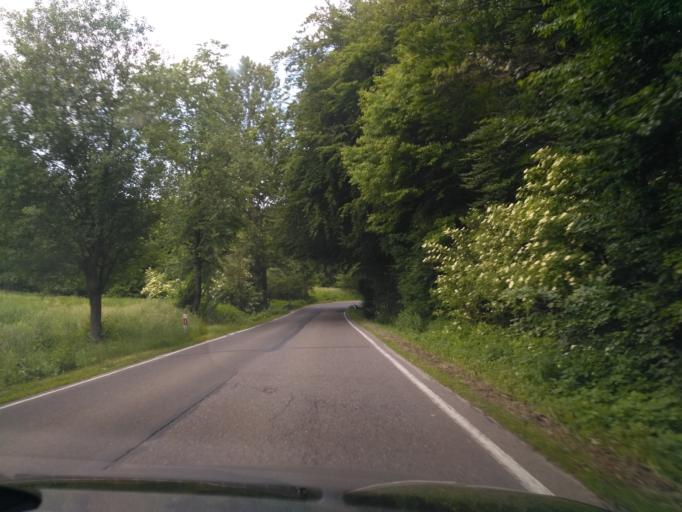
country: PL
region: Subcarpathian Voivodeship
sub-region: Powiat rzeszowski
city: Hyzne
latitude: 49.9423
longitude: 22.1900
